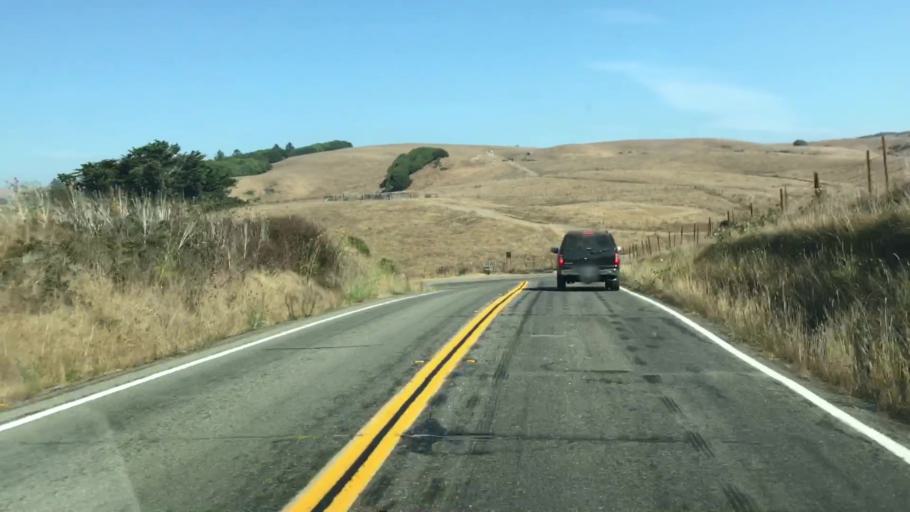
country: US
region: California
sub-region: Marin County
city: Lagunitas-Forest Knolls
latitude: 38.0464
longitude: -122.7714
